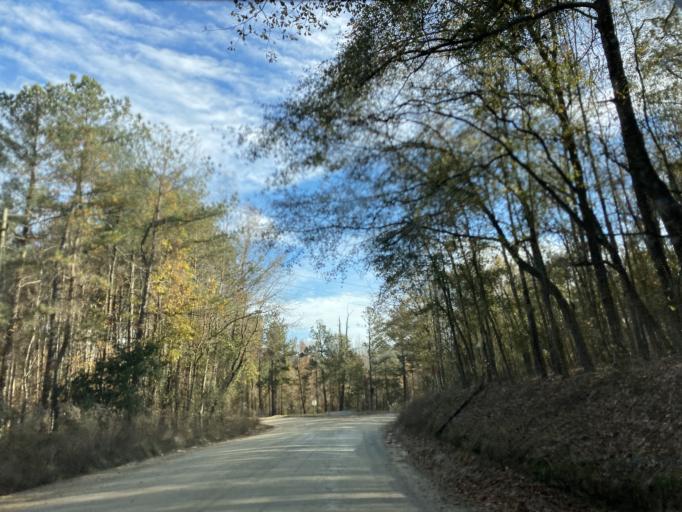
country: US
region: Georgia
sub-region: Jones County
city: Gray
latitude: 32.9111
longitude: -83.4885
